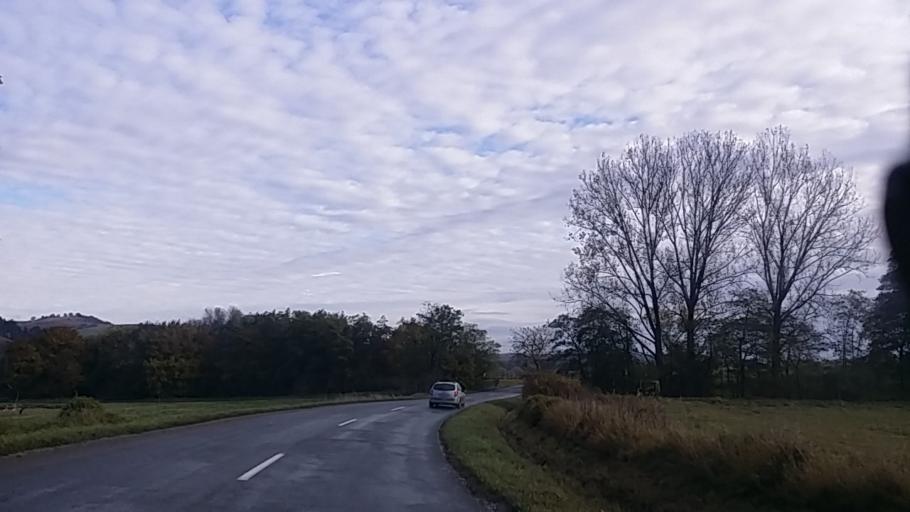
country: HU
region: Heves
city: Szilvasvarad
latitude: 48.1243
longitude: 20.3954
